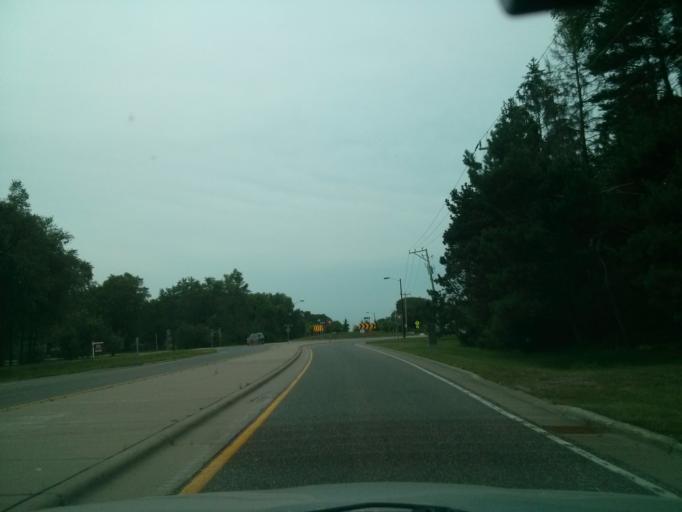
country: US
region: Minnesota
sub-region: Washington County
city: Lakeland
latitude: 44.9561
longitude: -92.7709
